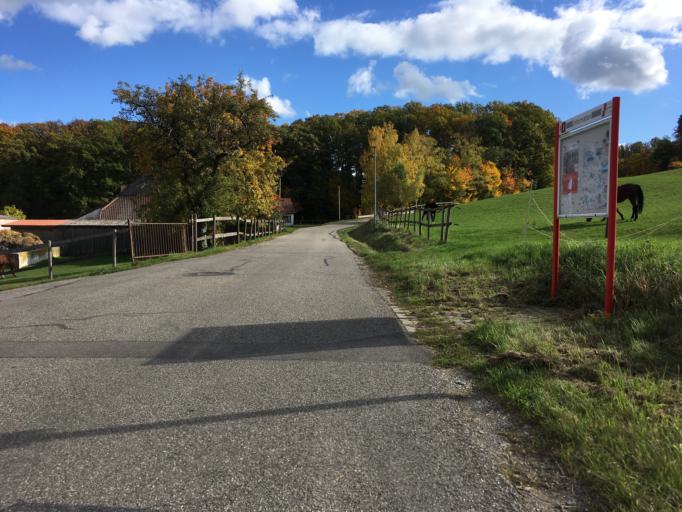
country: DE
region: Baden-Wuerttemberg
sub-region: Regierungsbezirk Stuttgart
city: Waldenburg
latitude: 49.1881
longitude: 9.6679
